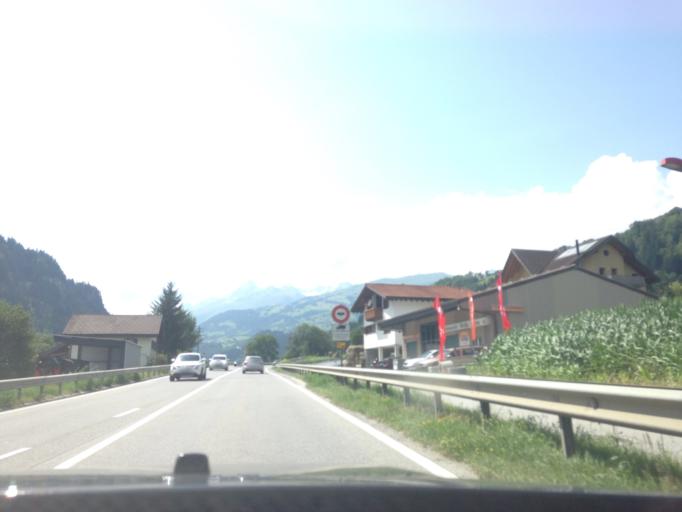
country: CH
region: Grisons
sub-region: Surselva District
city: Ilanz
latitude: 46.7749
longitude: 9.1771
